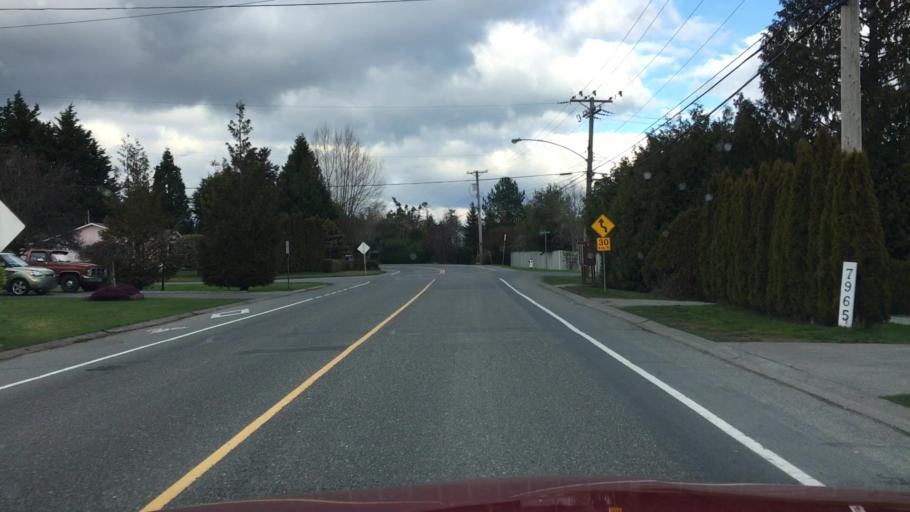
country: CA
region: British Columbia
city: North Saanich
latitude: 48.5984
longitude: -123.3946
